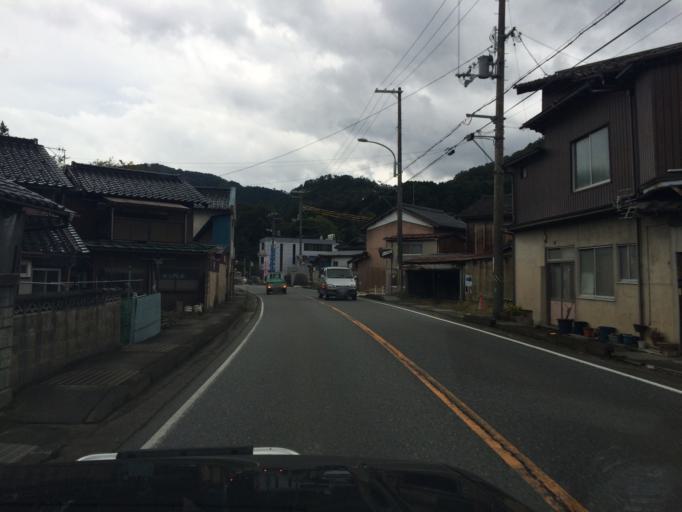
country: JP
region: Hyogo
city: Toyooka
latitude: 35.4054
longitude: 134.7774
